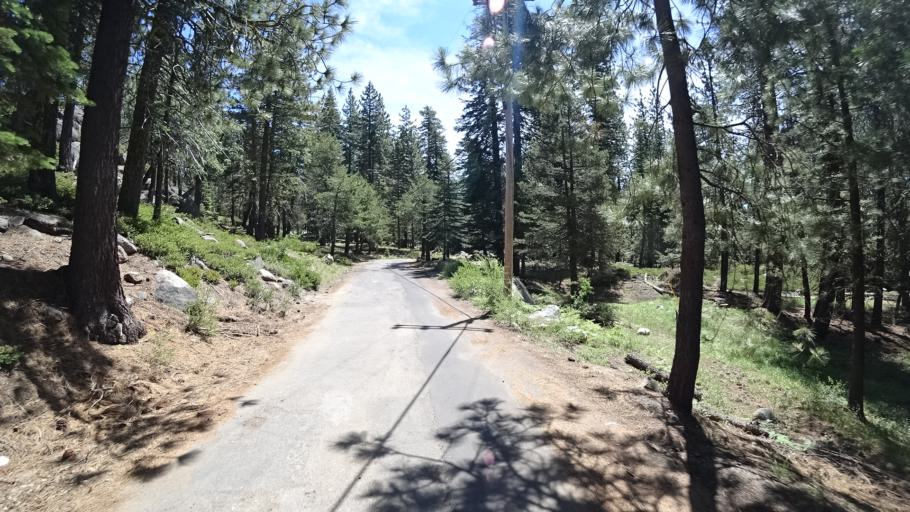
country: US
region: California
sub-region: Calaveras County
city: Arnold
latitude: 38.4225
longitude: -120.0972
